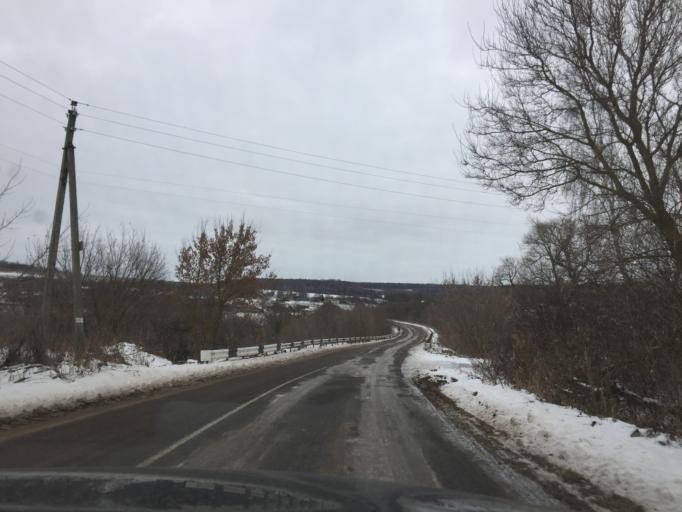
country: RU
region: Tula
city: Teploye
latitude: 53.7760
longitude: 37.6383
